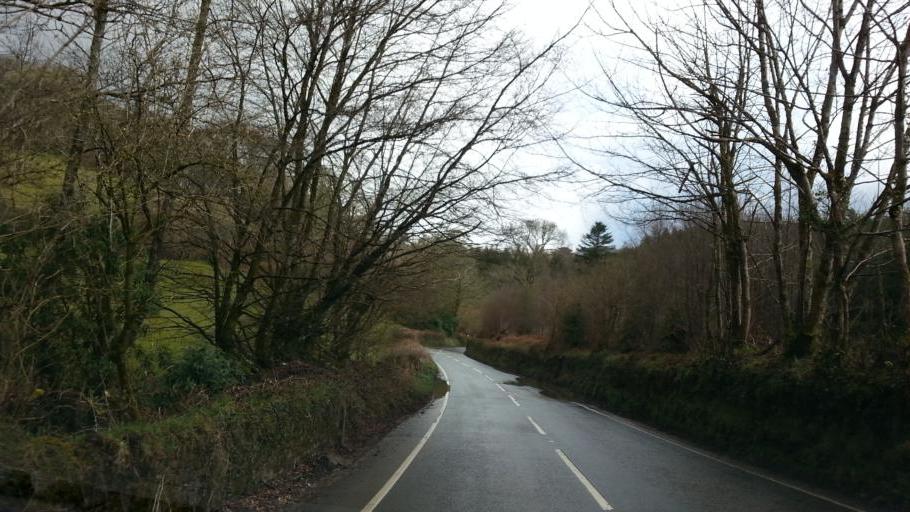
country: GB
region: England
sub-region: Devon
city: Combe Martin
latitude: 51.1456
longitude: -3.9977
